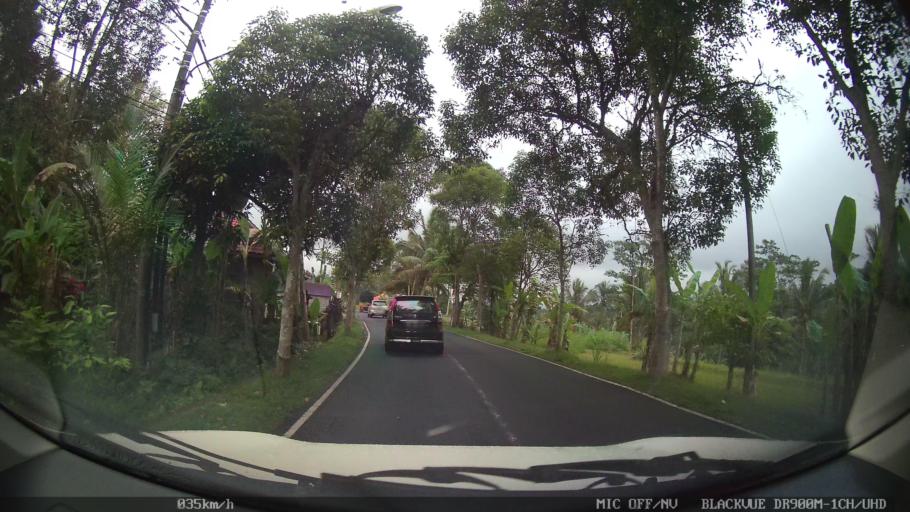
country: ID
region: Bali
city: Banjar Ponggang
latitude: -8.3950
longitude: 115.2531
